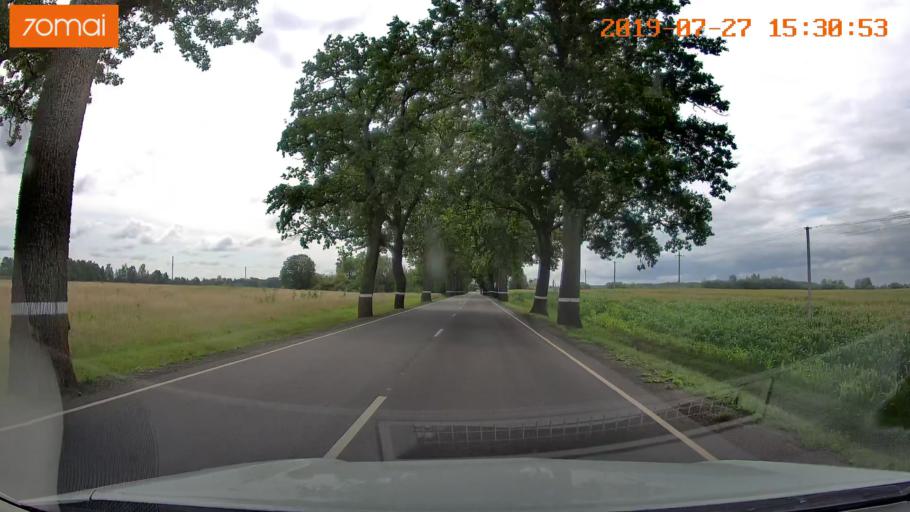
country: RU
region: Kaliningrad
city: Nesterov
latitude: 54.6258
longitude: 22.5028
